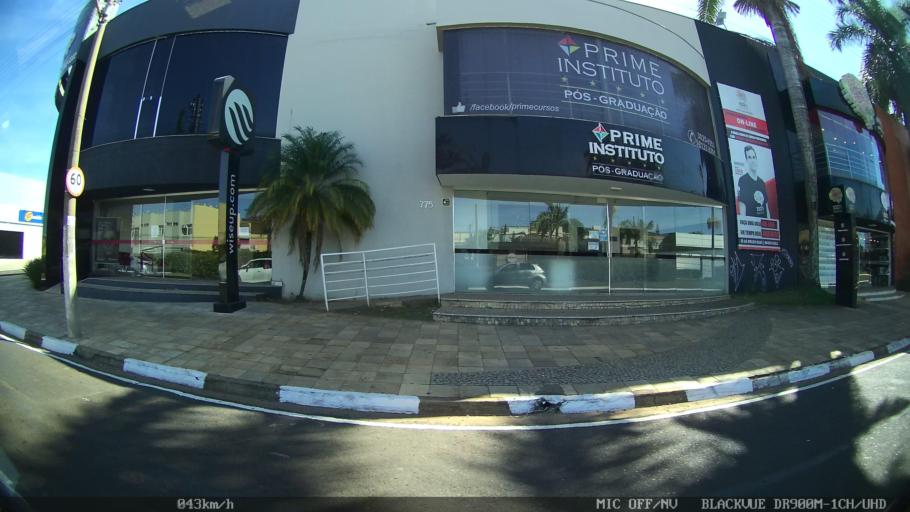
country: BR
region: Sao Paulo
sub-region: Franca
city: Franca
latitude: -20.5473
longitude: -47.4007
